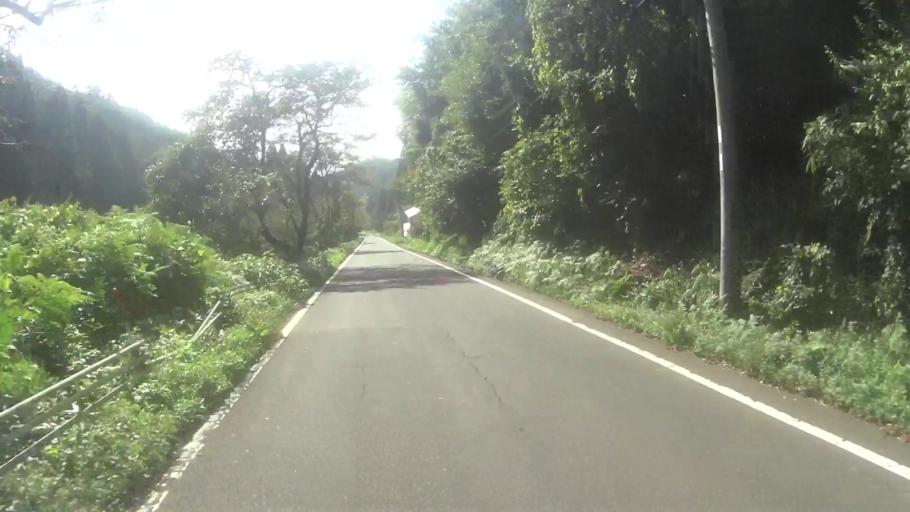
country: JP
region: Kyoto
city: Miyazu
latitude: 35.6880
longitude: 135.1152
